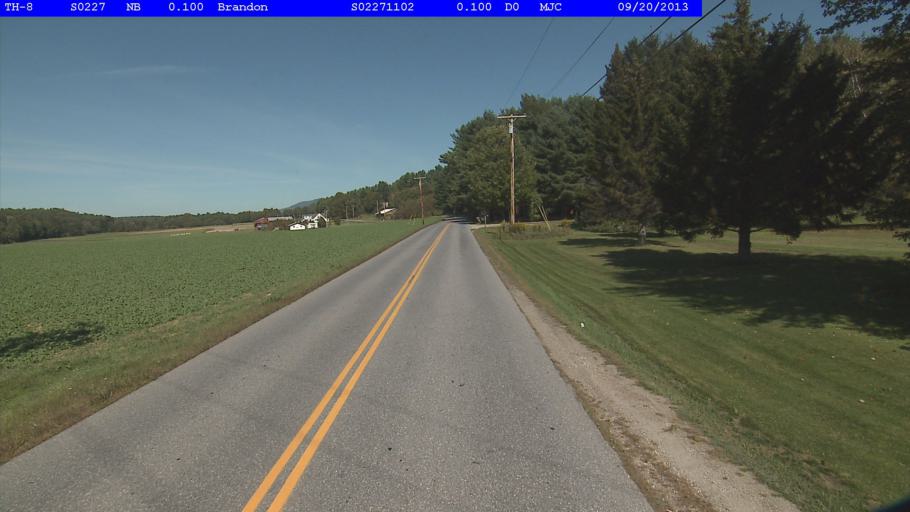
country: US
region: Vermont
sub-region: Rutland County
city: Brandon
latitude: 43.7759
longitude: -73.0527
